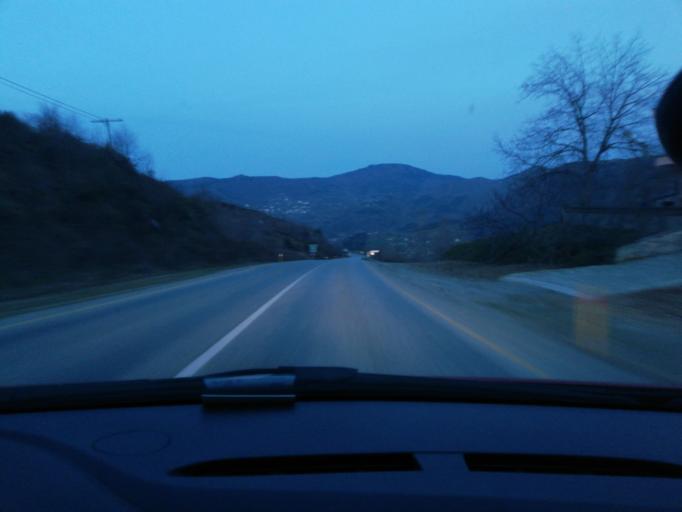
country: TR
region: Kastamonu
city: Inebolu
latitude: 41.9330
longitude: 33.7480
